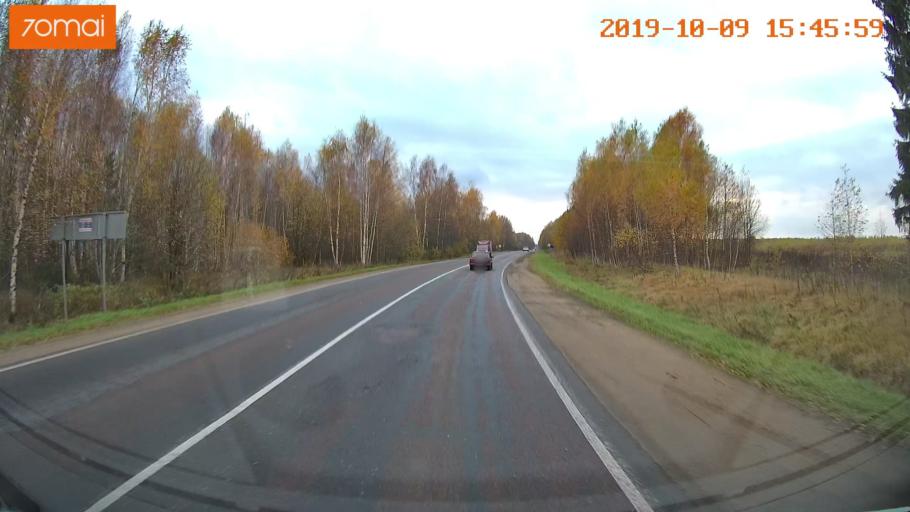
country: RU
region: Kostroma
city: Oktyabr'skiy
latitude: 57.8287
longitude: 41.0521
